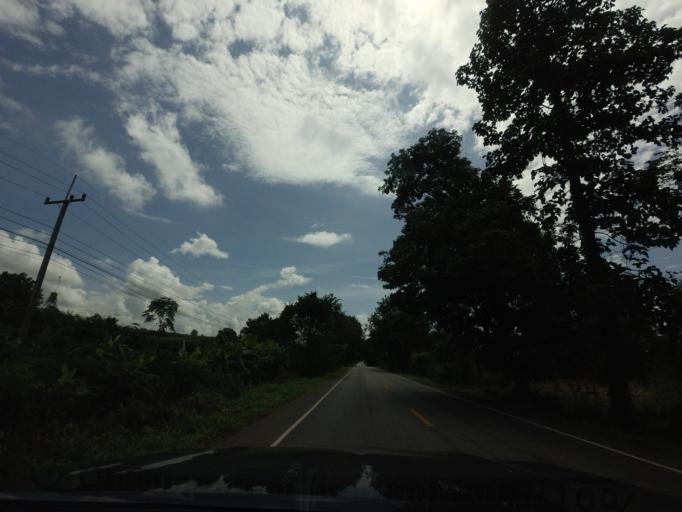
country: TH
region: Nong Khai
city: Pho Tak
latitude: 17.8051
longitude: 102.3416
